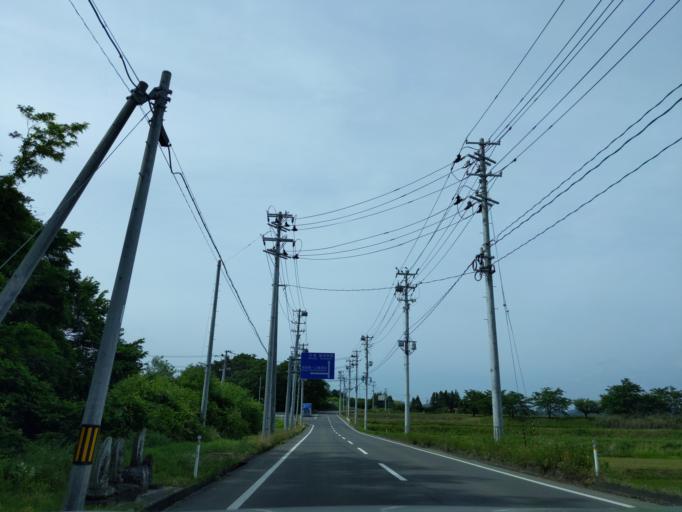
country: JP
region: Fukushima
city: Koriyama
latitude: 37.4590
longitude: 140.3126
